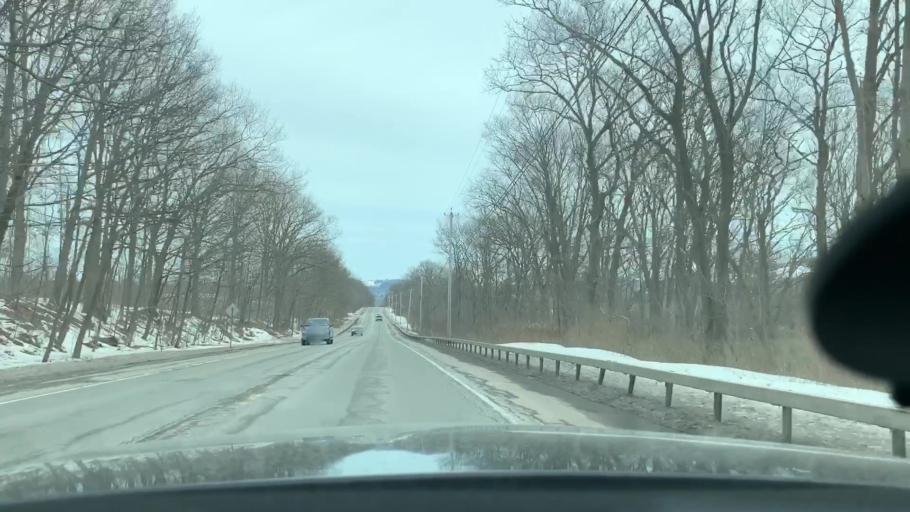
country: US
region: New York
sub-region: Herkimer County
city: Herkimer
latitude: 43.0246
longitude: -74.9366
